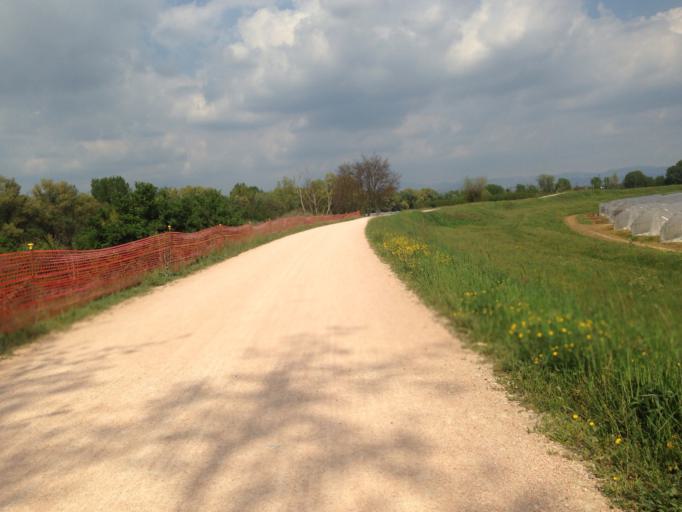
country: IT
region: Veneto
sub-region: Provincia di Verona
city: Campagnola
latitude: 45.3829
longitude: 11.0743
